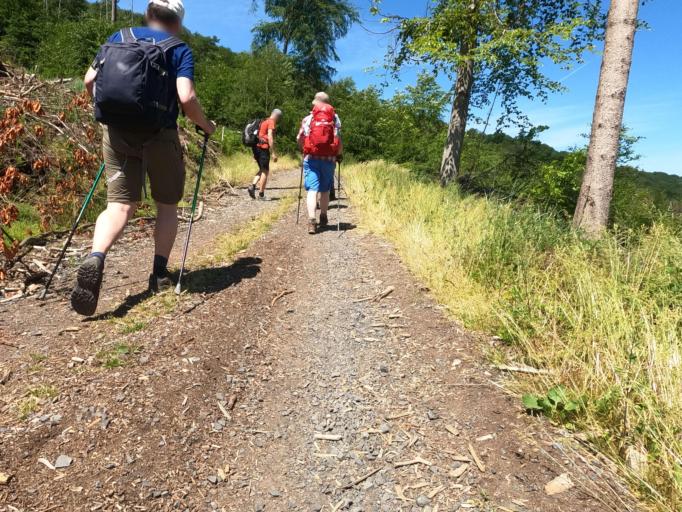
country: DE
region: Rheinland-Pfalz
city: Alpenrod
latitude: 50.6509
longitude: 7.8693
